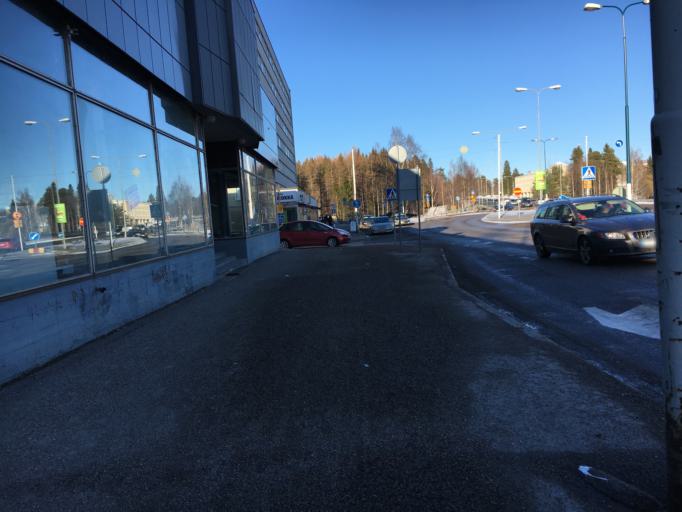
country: FI
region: Kainuu
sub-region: Kajaani
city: Kajaani
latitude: 64.2249
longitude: 27.7342
